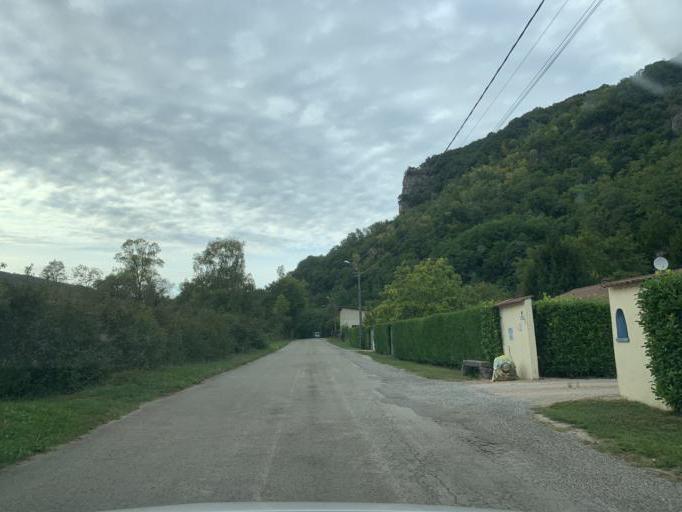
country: FR
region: Rhone-Alpes
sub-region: Departement de l'Ain
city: Vaux-en-Bugey
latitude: 45.9282
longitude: 5.3904
